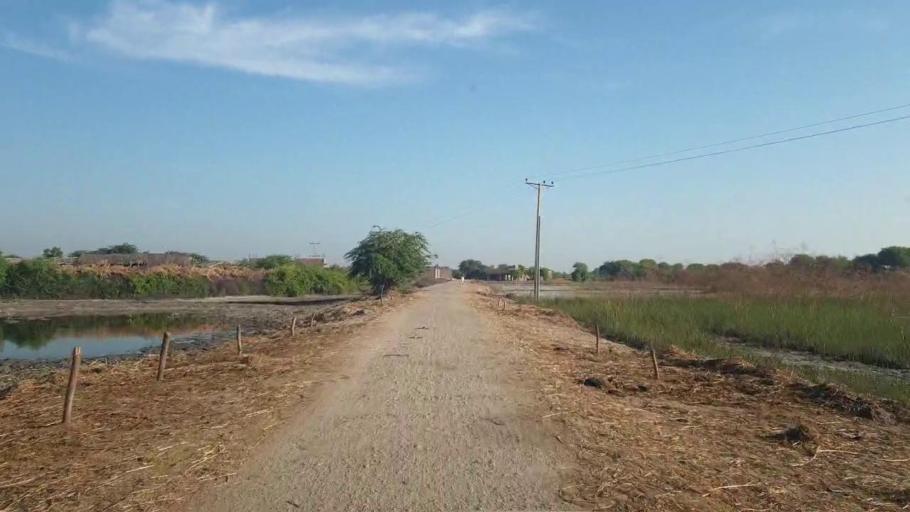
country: PK
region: Sindh
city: Talhar
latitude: 24.8148
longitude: 68.8393
